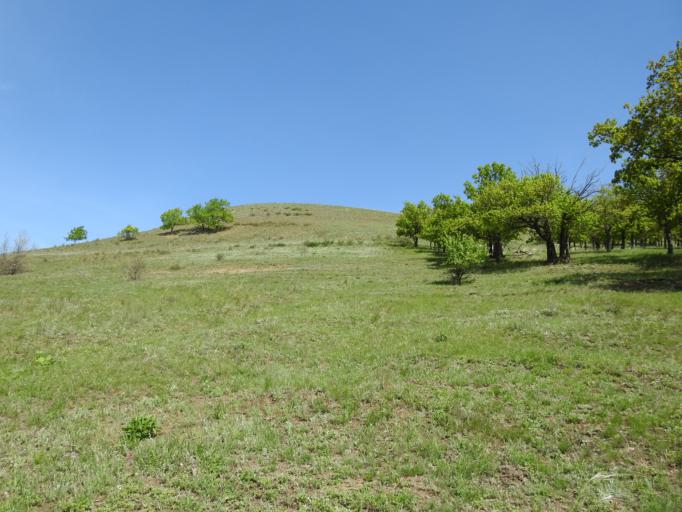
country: RU
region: Saratov
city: Krasnyy Oktyabr'
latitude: 51.5956
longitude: 45.7221
